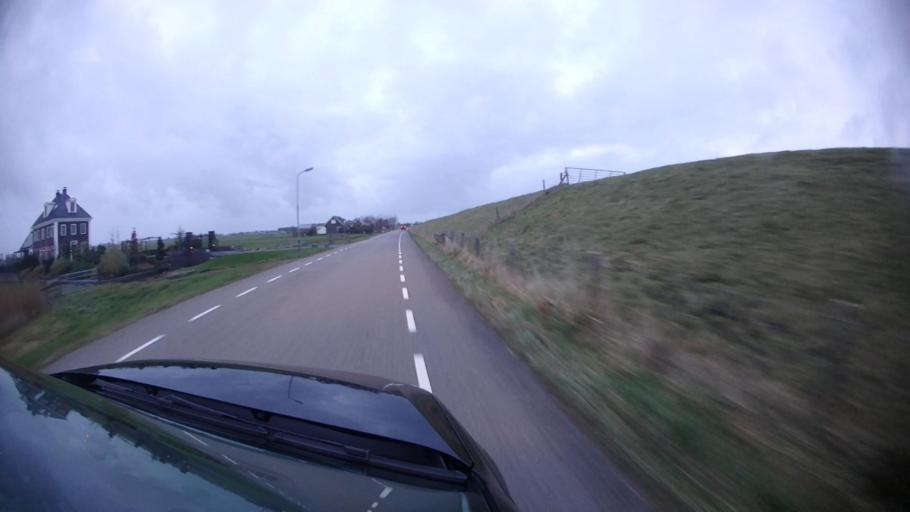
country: NL
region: North Holland
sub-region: Gemeente Edam-Volendam
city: Volendam
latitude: 52.4801
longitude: 5.0589
